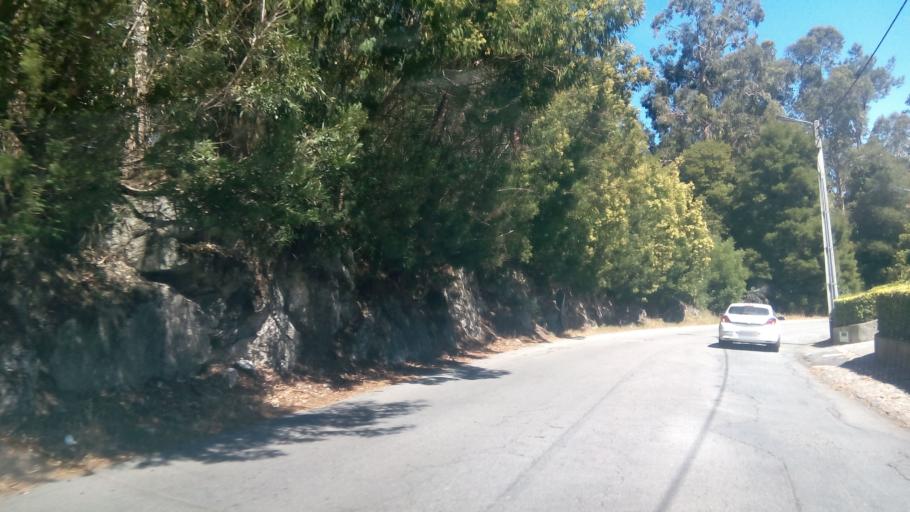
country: PT
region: Porto
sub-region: Paredes
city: Baltar
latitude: 41.1831
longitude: -8.3563
